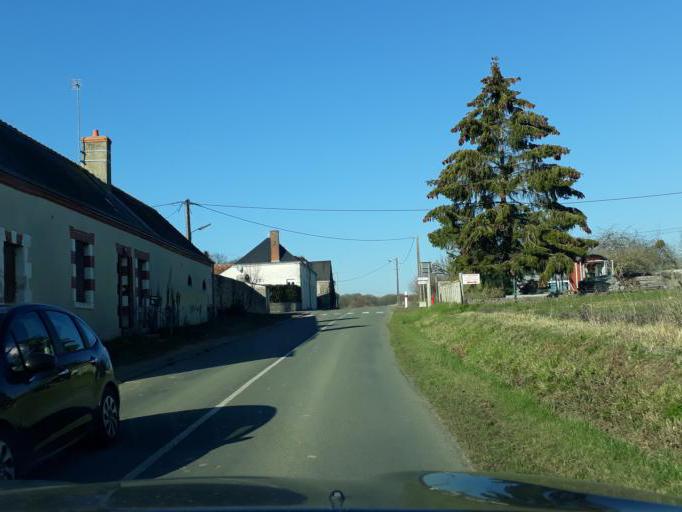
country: FR
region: Centre
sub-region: Departement du Loir-et-Cher
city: Oucques
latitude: 47.8390
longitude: 1.3813
